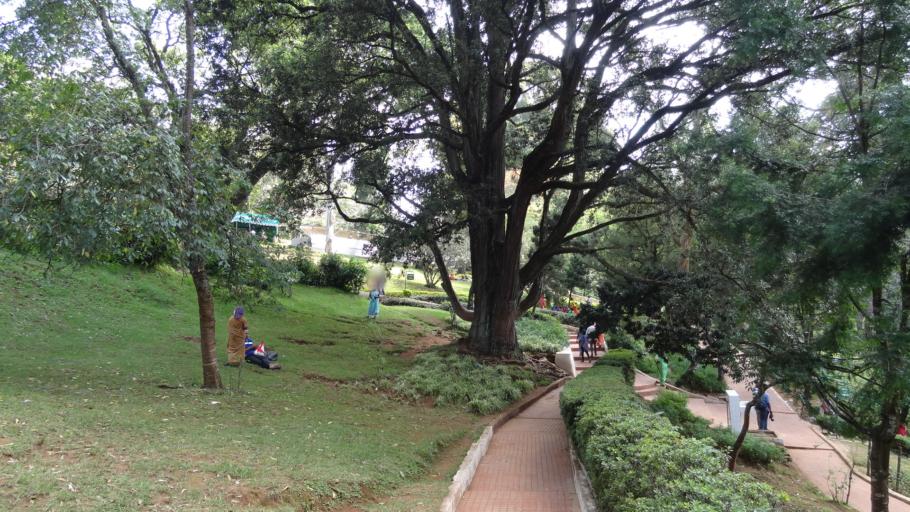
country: IN
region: Tamil Nadu
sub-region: Nilgiri
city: Wellington
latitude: 11.3557
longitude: 76.8001
